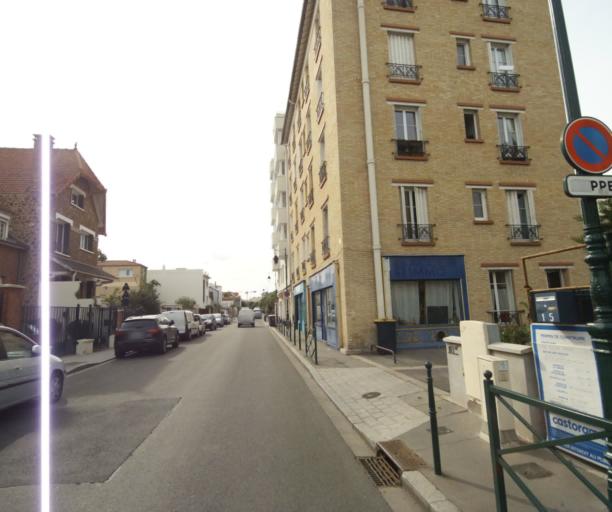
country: FR
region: Ile-de-France
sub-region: Departement des Hauts-de-Seine
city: Bois-Colombes
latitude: 48.9218
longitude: 2.2663
